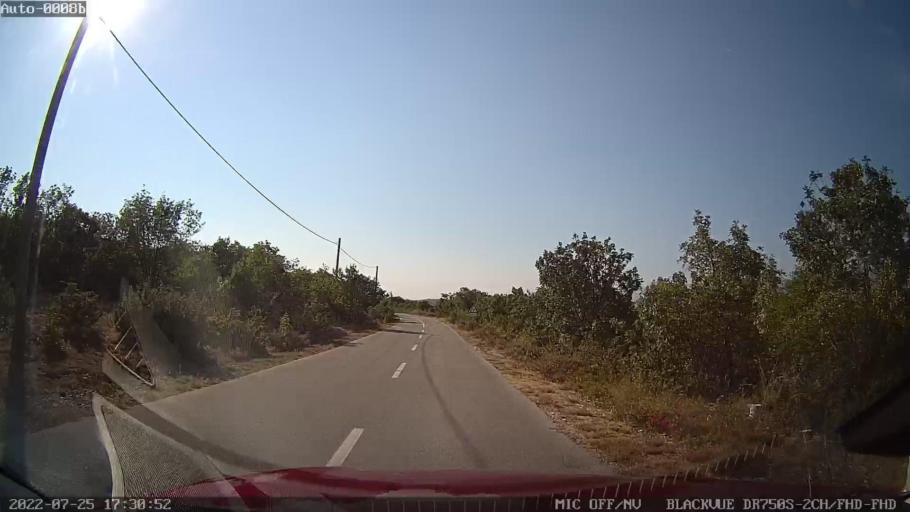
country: HR
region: Zadarska
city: Posedarje
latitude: 44.1668
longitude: 15.5046
